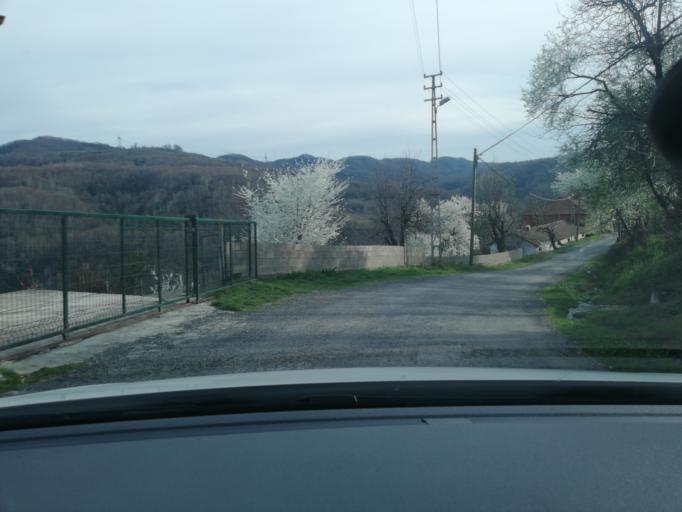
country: TR
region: Zonguldak
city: Kozlu
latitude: 41.3553
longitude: 31.6447
